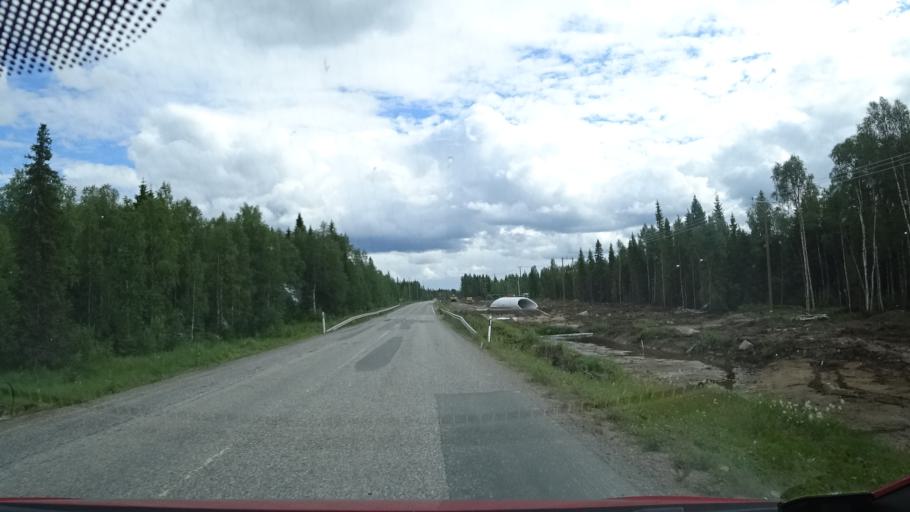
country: FI
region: Lapland
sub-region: Rovaniemi
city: Rovaniemi
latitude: 66.5393
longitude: 25.7205
